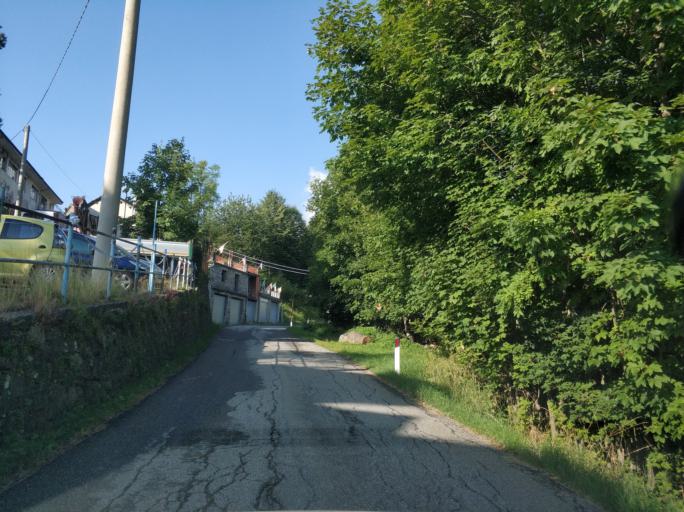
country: IT
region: Piedmont
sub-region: Provincia di Torino
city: Viu
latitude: 45.2168
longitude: 7.3784
